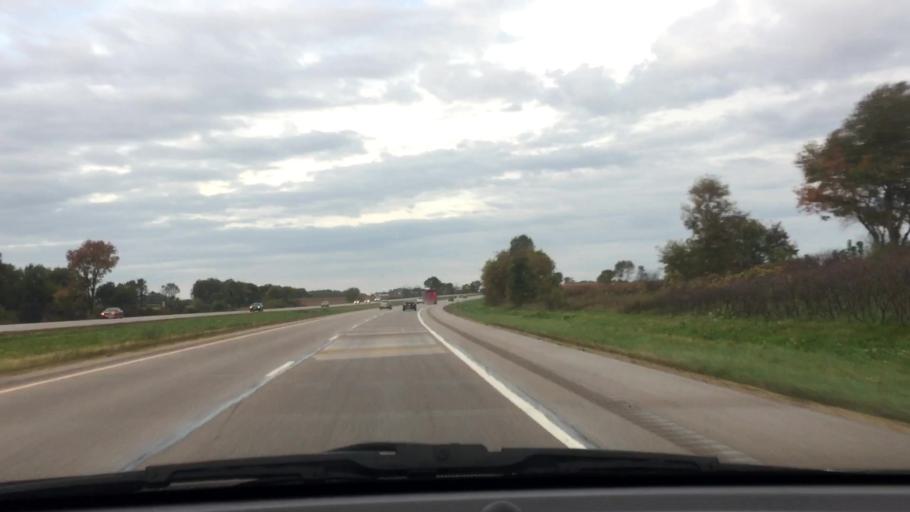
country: US
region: Wisconsin
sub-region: Rock County
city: Clinton
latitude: 42.5743
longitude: -88.8046
